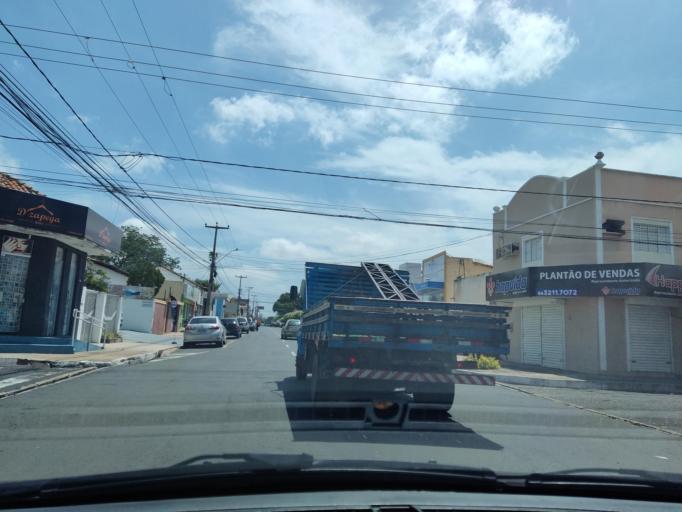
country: BR
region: Piaui
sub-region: Teresina
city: Teresina
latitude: -5.0843
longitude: -42.8157
